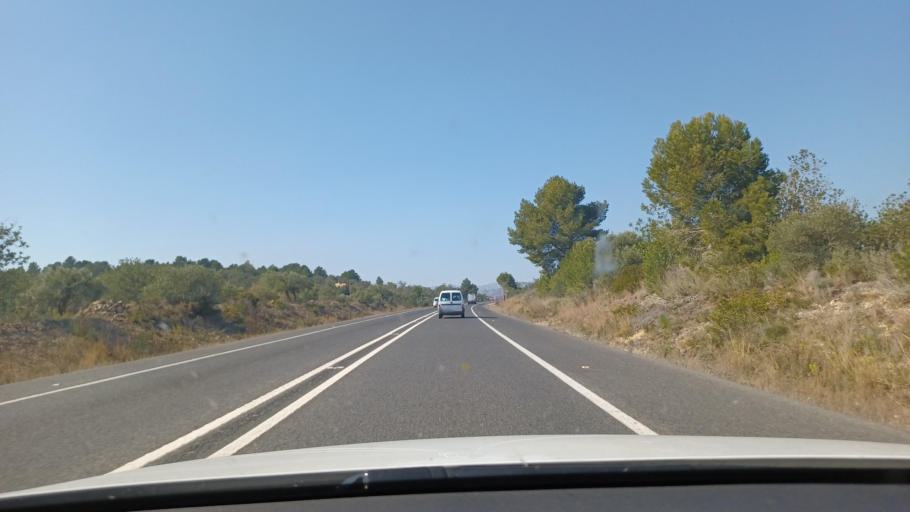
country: ES
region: Catalonia
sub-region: Provincia de Tarragona
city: l'Ametlla de Mar
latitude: 40.8952
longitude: 0.7589
